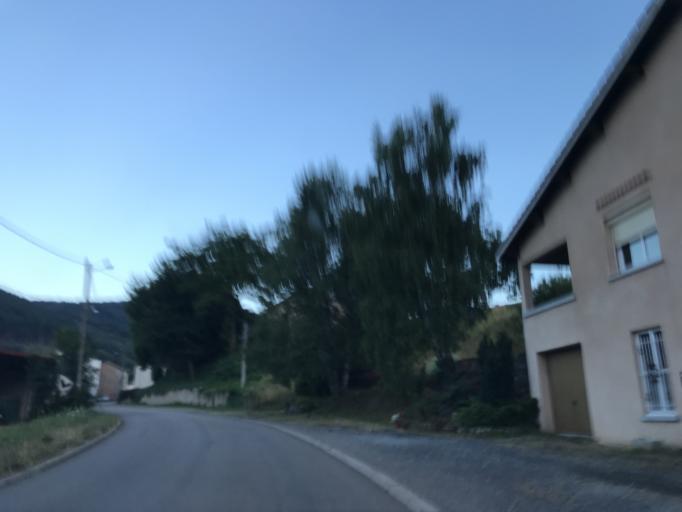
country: FR
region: Auvergne
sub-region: Departement du Puy-de-Dome
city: Celles-sur-Durolle
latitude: 45.8299
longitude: 3.6745
